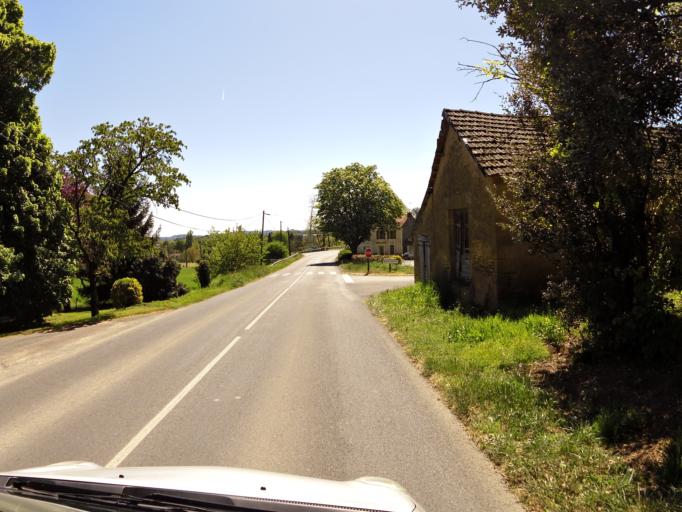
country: FR
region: Aquitaine
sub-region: Departement de la Dordogne
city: Sarlat-la-Caneda
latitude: 44.9613
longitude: 1.2583
